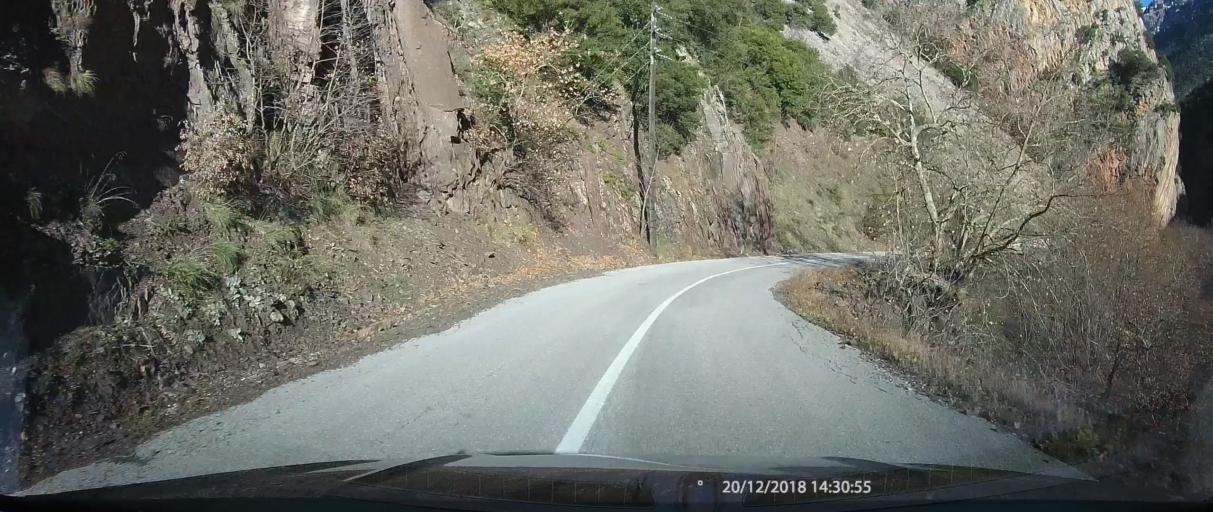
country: GR
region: Central Greece
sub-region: Nomos Evrytanias
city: Karpenisi
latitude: 38.7911
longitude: 21.6983
